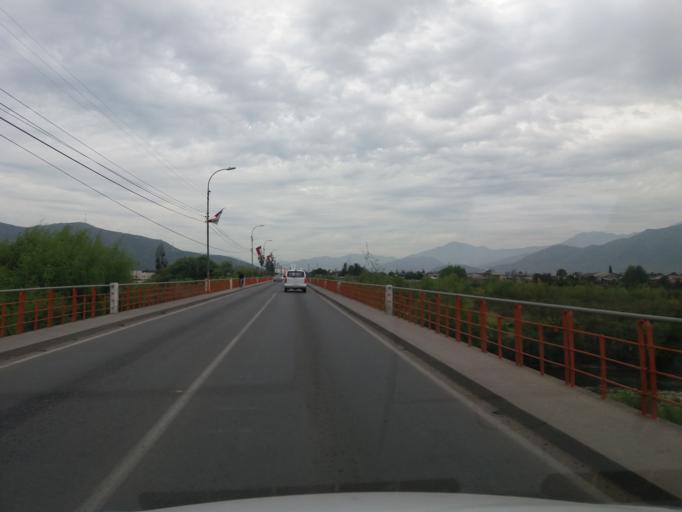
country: CL
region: Valparaiso
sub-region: Provincia de Quillota
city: Hacienda La Calera
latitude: -32.7813
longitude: -71.1909
